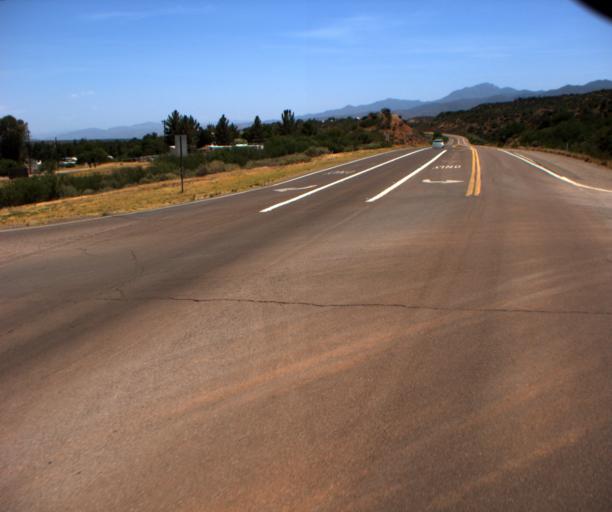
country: US
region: Arizona
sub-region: Gila County
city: Tonto Basin
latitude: 33.8768
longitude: -111.3158
